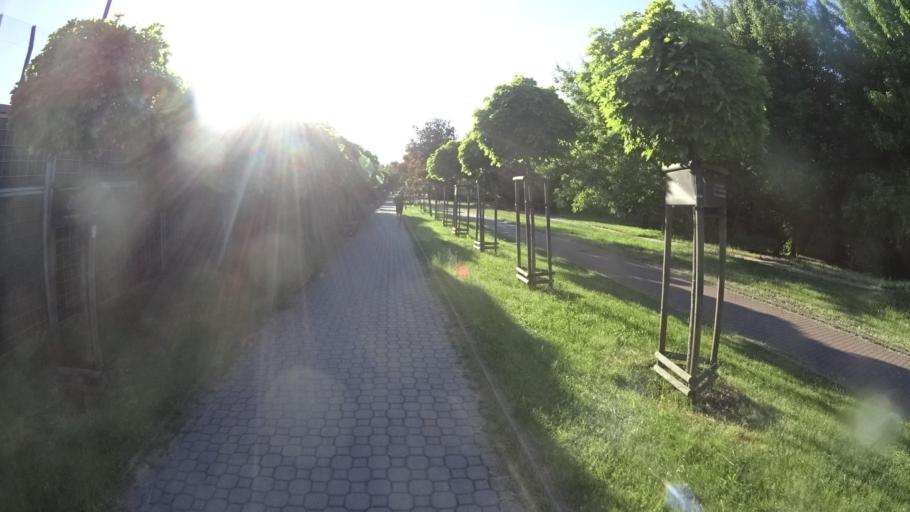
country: PL
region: Masovian Voivodeship
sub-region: Warszawa
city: Bielany
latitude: 52.2639
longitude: 20.9499
